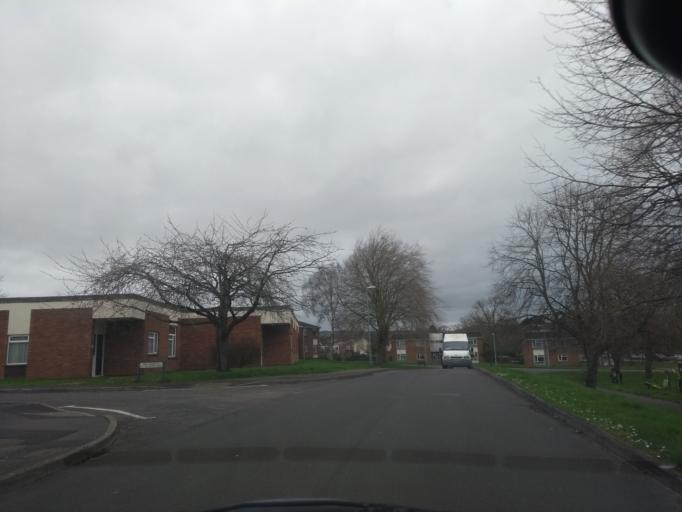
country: GB
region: England
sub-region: Somerset
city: Taunton
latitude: 51.0313
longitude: -3.0949
